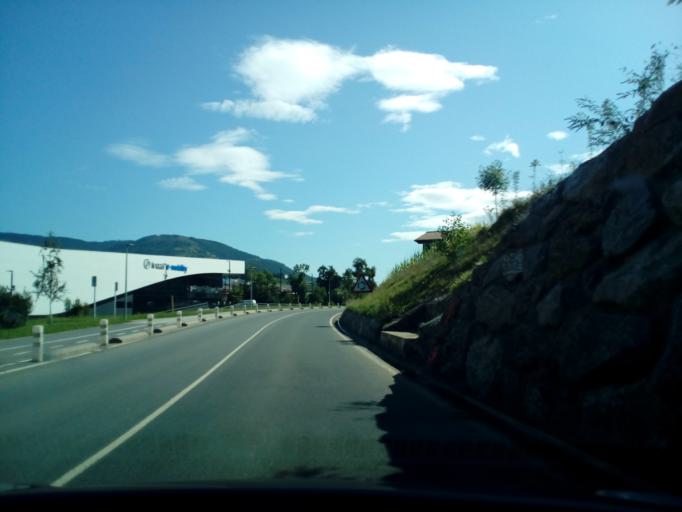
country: ES
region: Basque Country
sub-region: Provincia de Guipuzcoa
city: Aduna
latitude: 43.2067
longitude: -2.0405
